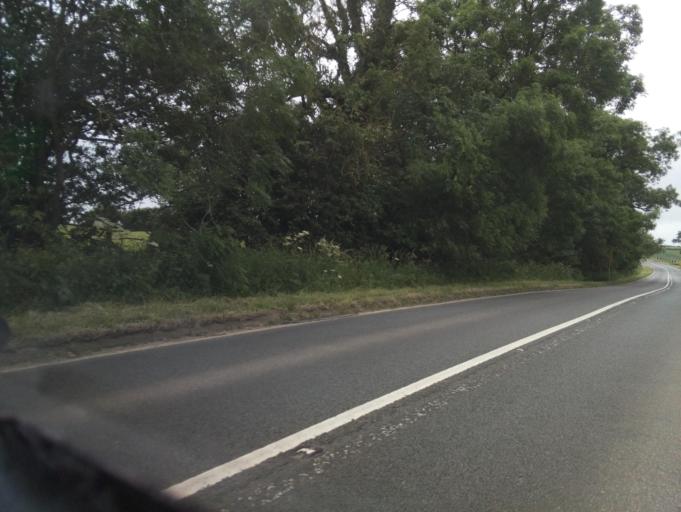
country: GB
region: England
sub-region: Leicestershire
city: Houghton on the Hill
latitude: 52.6045
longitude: -0.8777
